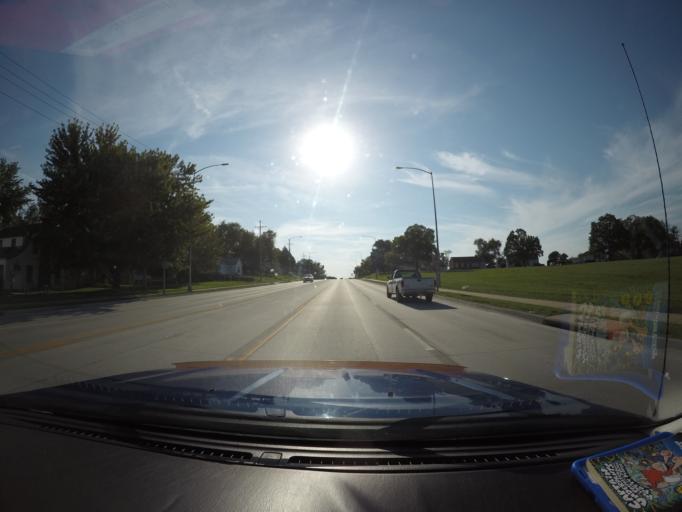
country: US
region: Kansas
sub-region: Leavenworth County
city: Leavenworth
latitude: 39.3282
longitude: -94.9258
